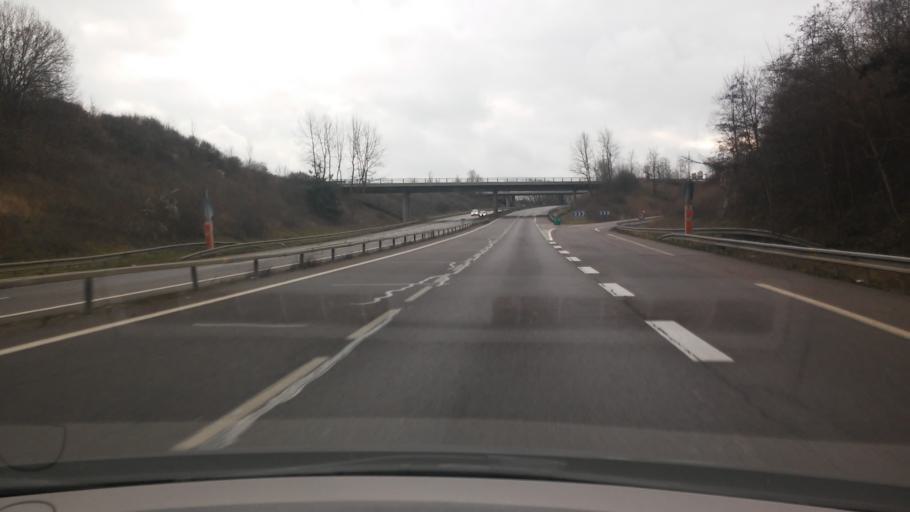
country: FR
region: Lorraine
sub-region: Departement de la Moselle
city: Saint-Julien-les-Metz
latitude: 49.1285
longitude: 6.2416
